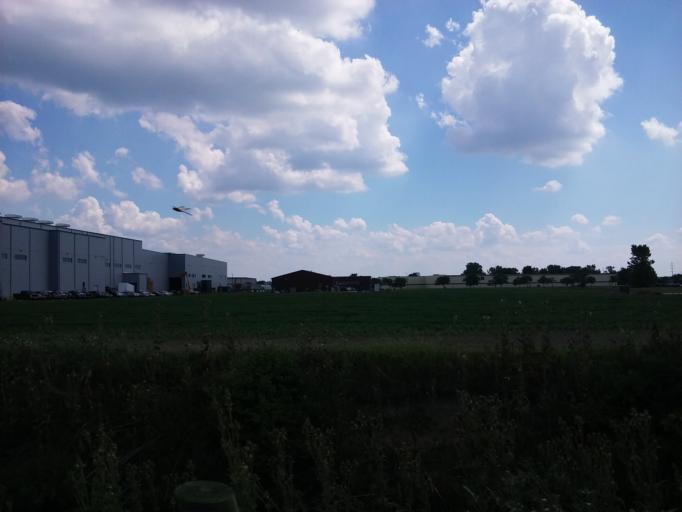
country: US
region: Ohio
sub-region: Wood County
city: Bowling Green
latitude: 41.3851
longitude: -83.6079
